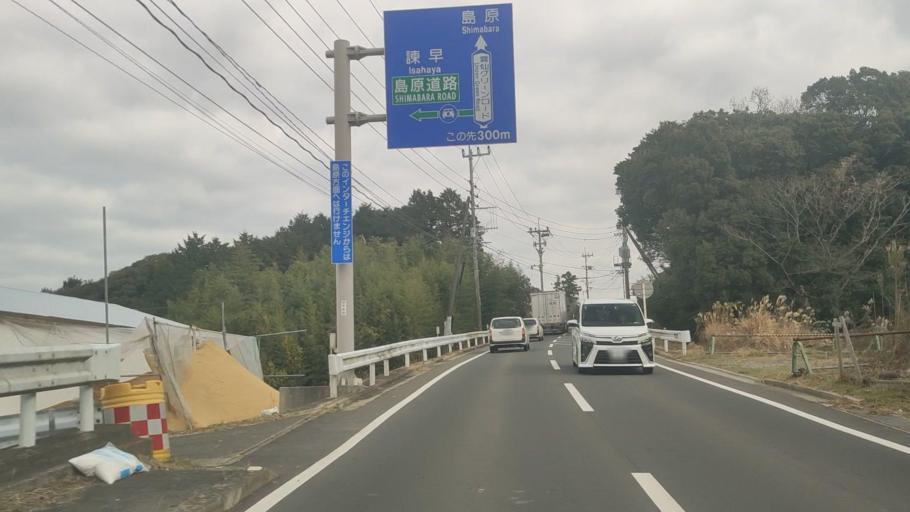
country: JP
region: Nagasaki
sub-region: Isahaya-shi
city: Isahaya
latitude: 32.8155
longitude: 130.1735
